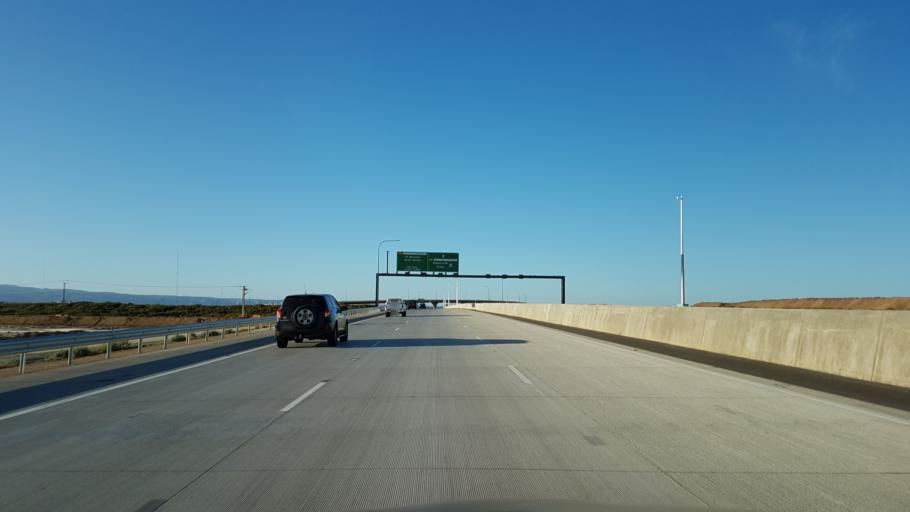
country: AU
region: South Australia
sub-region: Port Adelaide Enfield
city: Blair Athol
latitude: -34.8220
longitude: 138.5623
